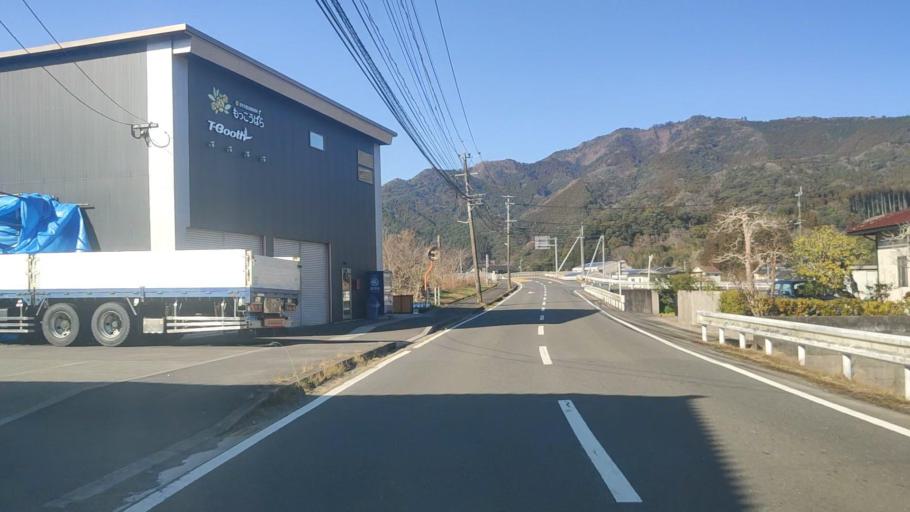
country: JP
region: Oita
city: Saiki
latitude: 32.9774
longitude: 131.8514
